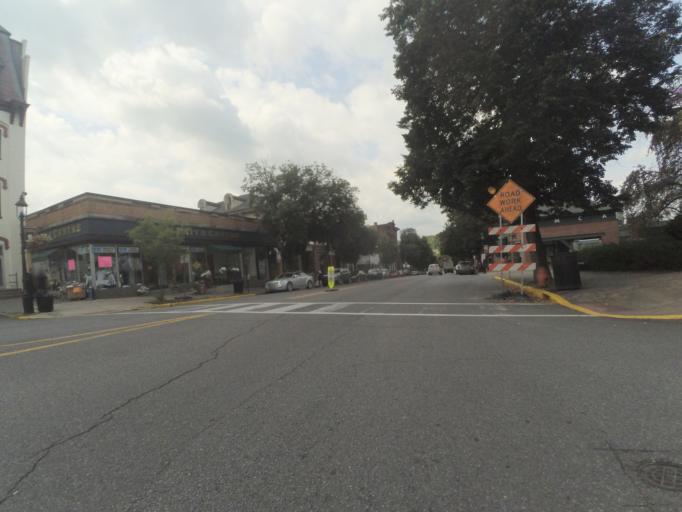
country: US
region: Pennsylvania
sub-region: Centre County
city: Bellefonte
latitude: 40.9120
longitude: -77.7782
